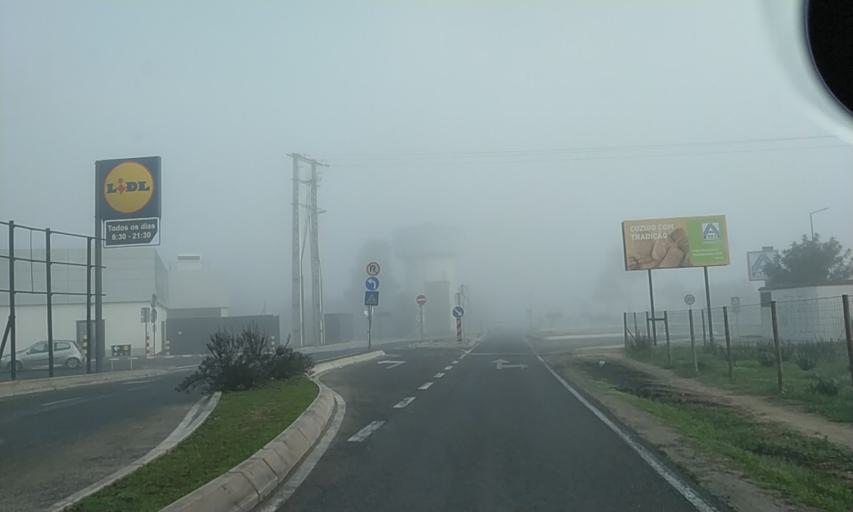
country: PT
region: Setubal
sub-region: Palmela
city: Pinhal Novo
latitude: 38.6187
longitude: -8.9173
